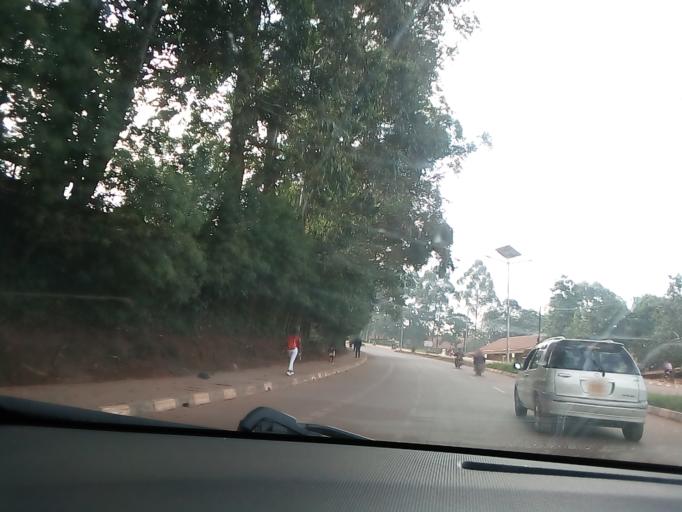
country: UG
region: Central Region
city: Masaka
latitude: -0.3492
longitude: 31.7339
